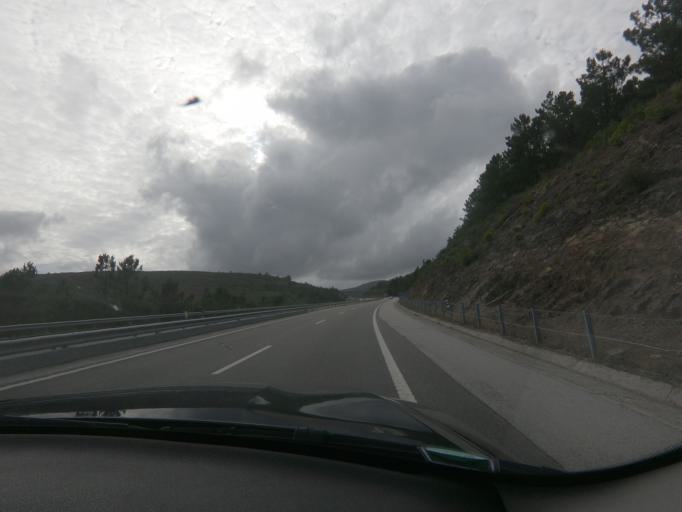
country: PT
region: Viseu
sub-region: Lamego
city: Lamego
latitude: 41.0482
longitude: -7.8462
